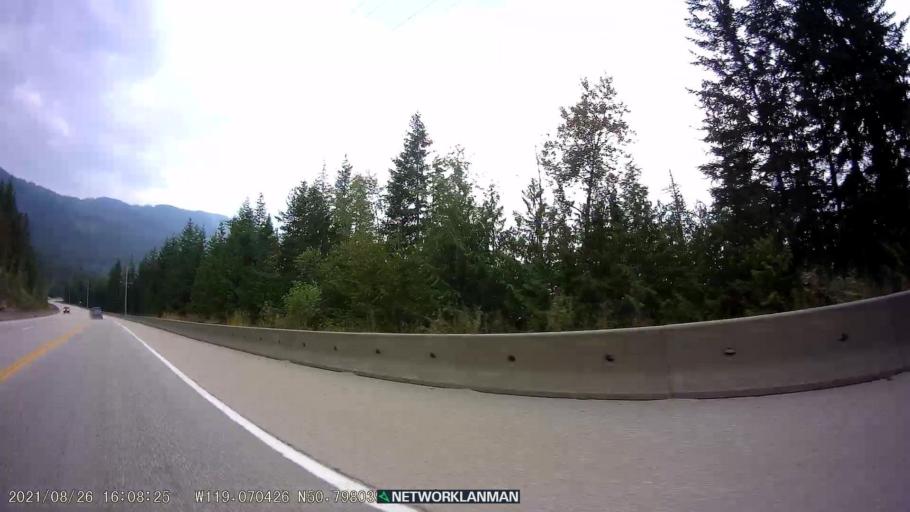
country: CA
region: British Columbia
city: Sicamous
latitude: 50.7978
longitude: -119.0707
